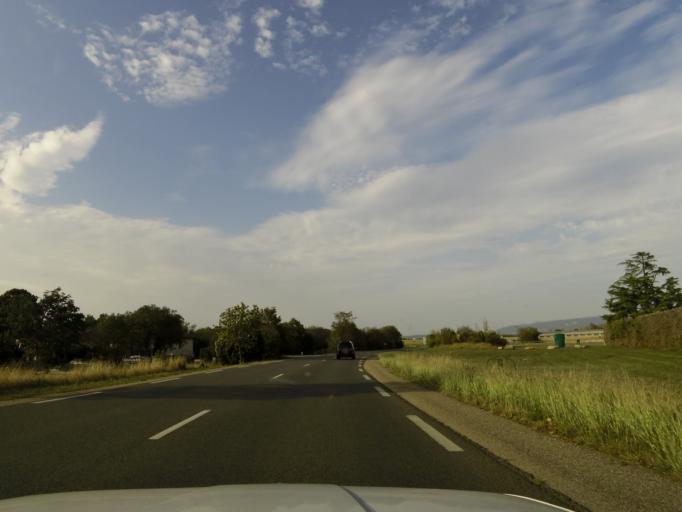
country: FR
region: Rhone-Alpes
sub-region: Departement de l'Isere
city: Hieres-sur-Amby
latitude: 45.8092
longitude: 5.2699
